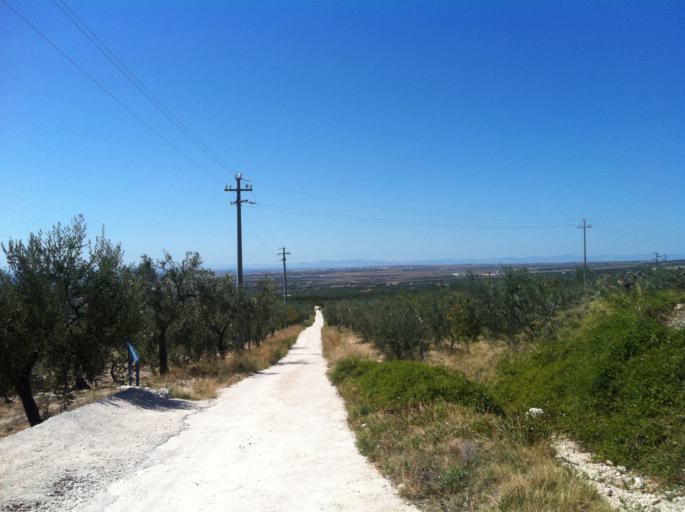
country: IT
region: Apulia
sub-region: Provincia di Foggia
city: Manfredonia
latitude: 41.6615
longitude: 15.9161
